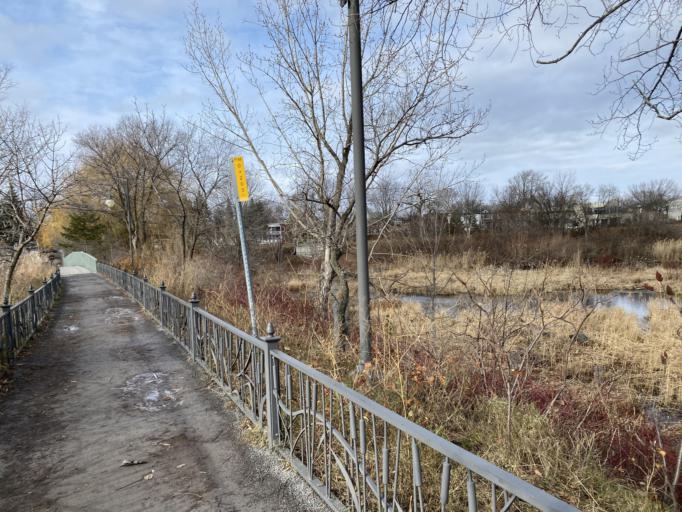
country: CA
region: Quebec
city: Saint-Raymond
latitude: 45.4287
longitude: -73.5913
